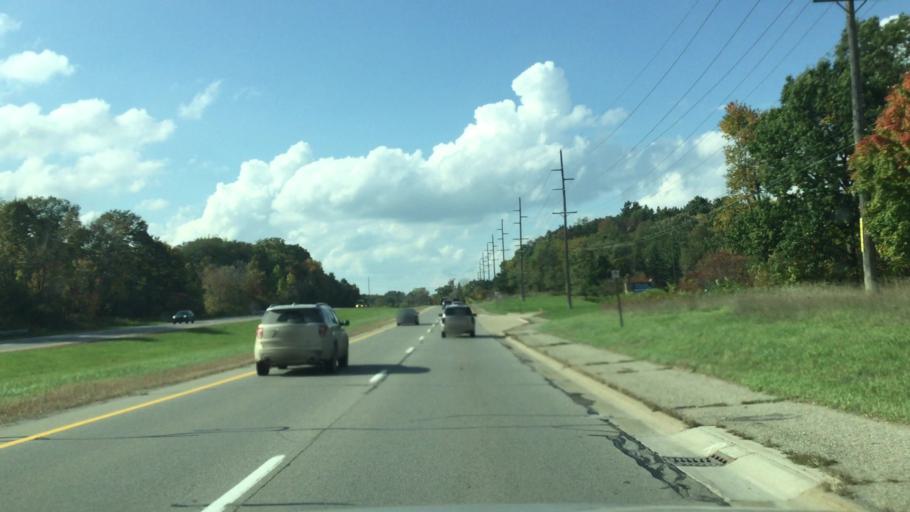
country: US
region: Michigan
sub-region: Oakland County
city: Milford
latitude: 42.6513
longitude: -83.5452
